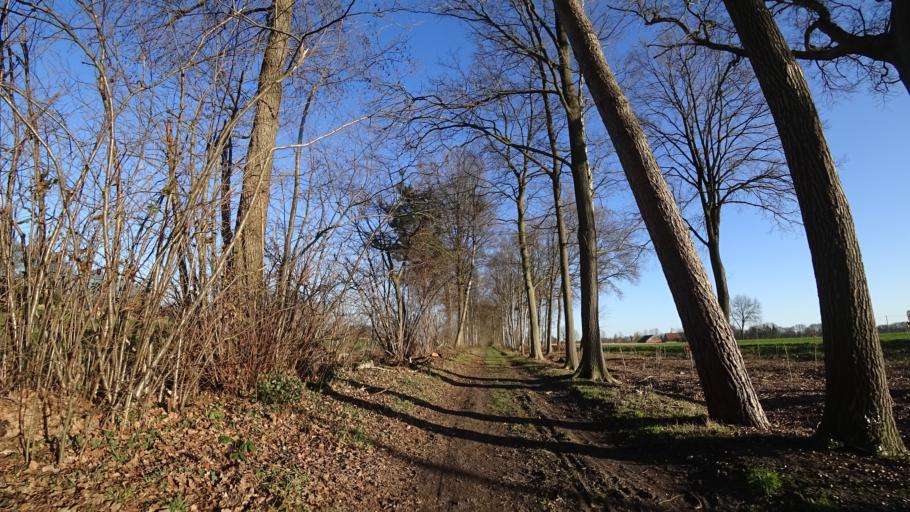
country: DE
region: North Rhine-Westphalia
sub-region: Regierungsbezirk Detmold
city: Guetersloh
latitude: 51.9319
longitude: 8.3313
